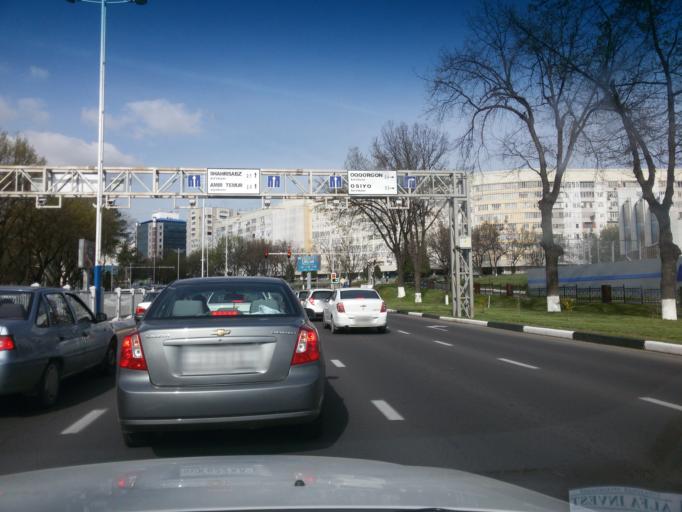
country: UZ
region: Toshkent
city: Salor
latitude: 41.3210
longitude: 69.3044
